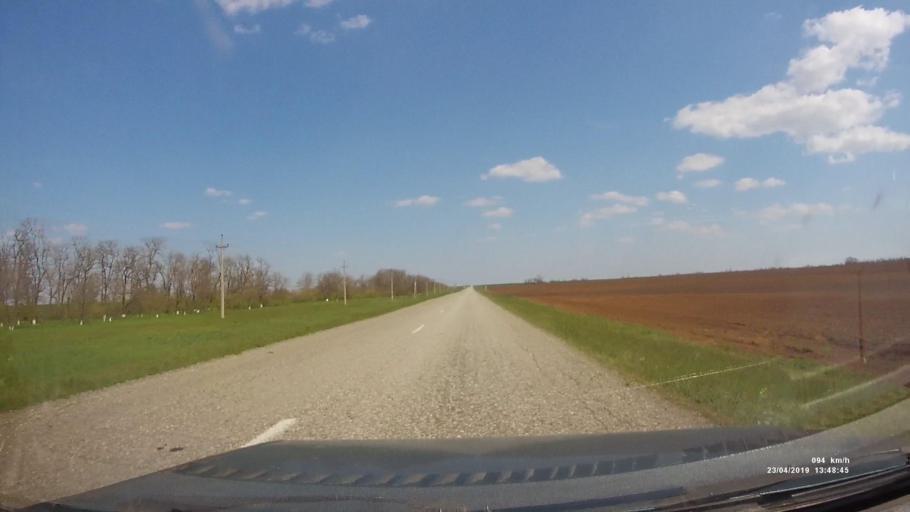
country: RU
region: Kalmykiya
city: Yashalta
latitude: 46.5992
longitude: 42.8811
